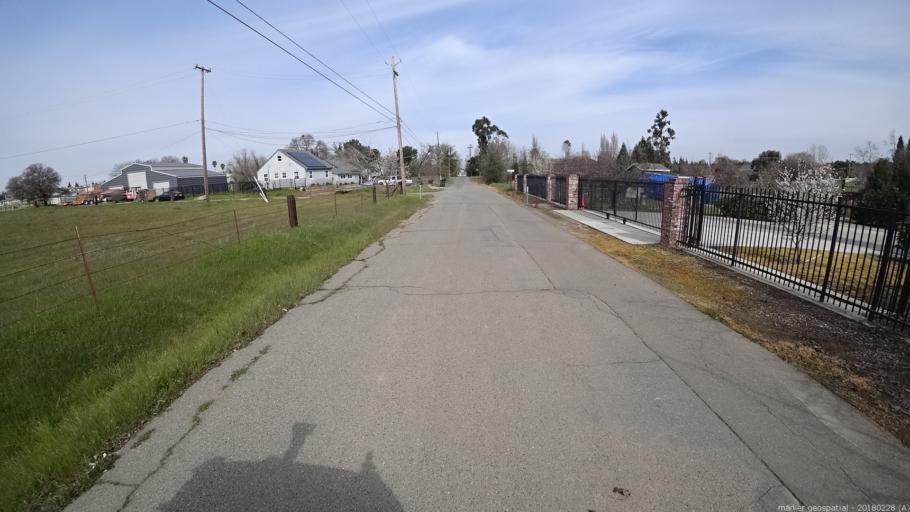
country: US
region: California
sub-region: Sacramento County
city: Antelope
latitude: 38.7159
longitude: -121.3322
